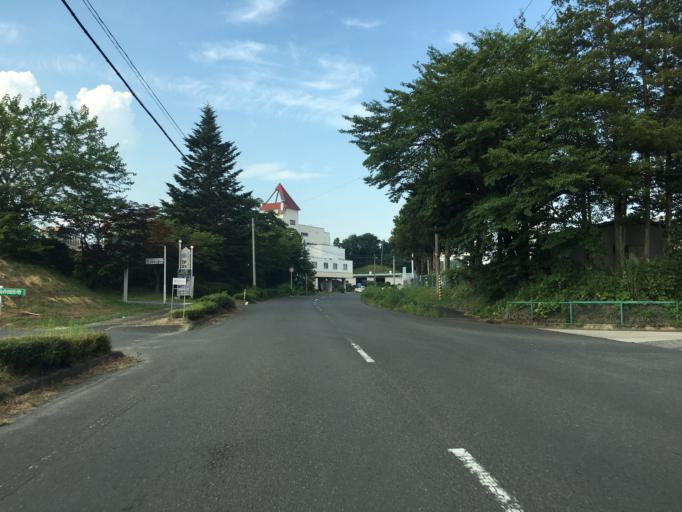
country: JP
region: Fukushima
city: Nihommatsu
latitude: 37.5822
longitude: 140.4378
